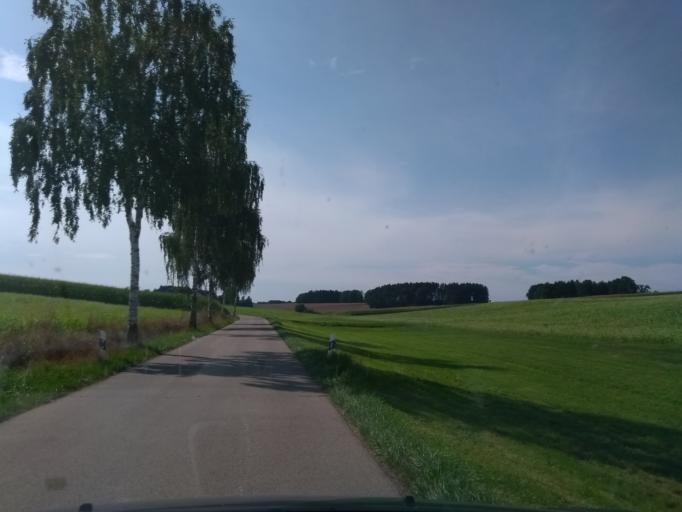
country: DE
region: Bavaria
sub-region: Upper Bavaria
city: Schwabhausen
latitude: 48.4017
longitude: 11.3653
